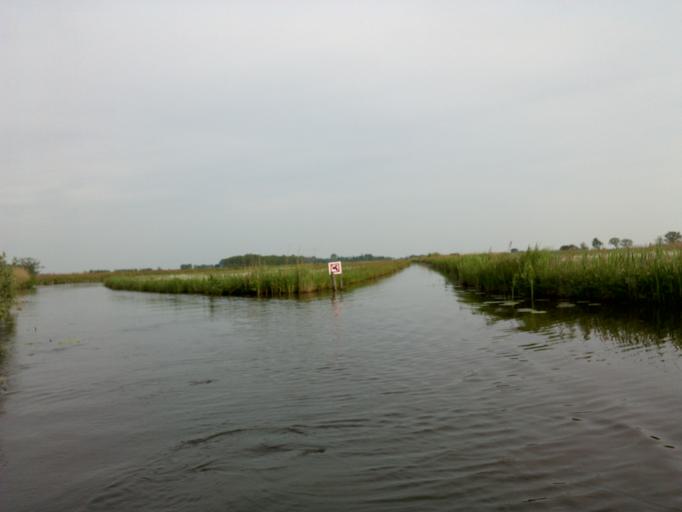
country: NL
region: South Holland
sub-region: Gemeente Nieuwkoop
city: Nieuwkoop
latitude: 52.1442
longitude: 4.7948
